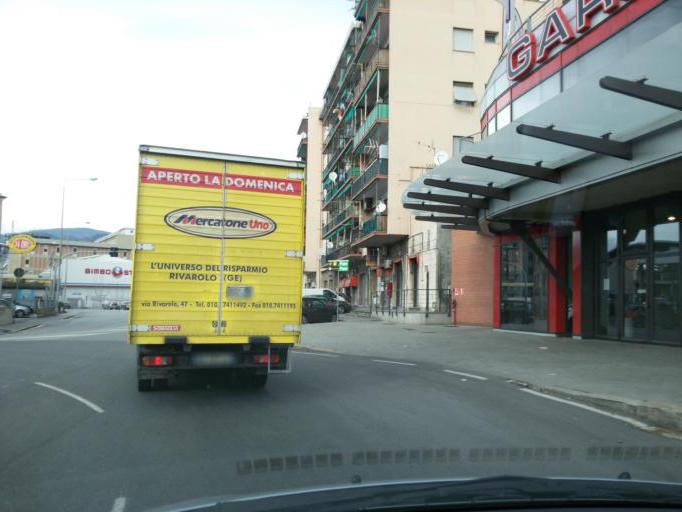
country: IT
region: Liguria
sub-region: Provincia di Genova
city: San Teodoro
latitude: 44.4193
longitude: 8.8593
